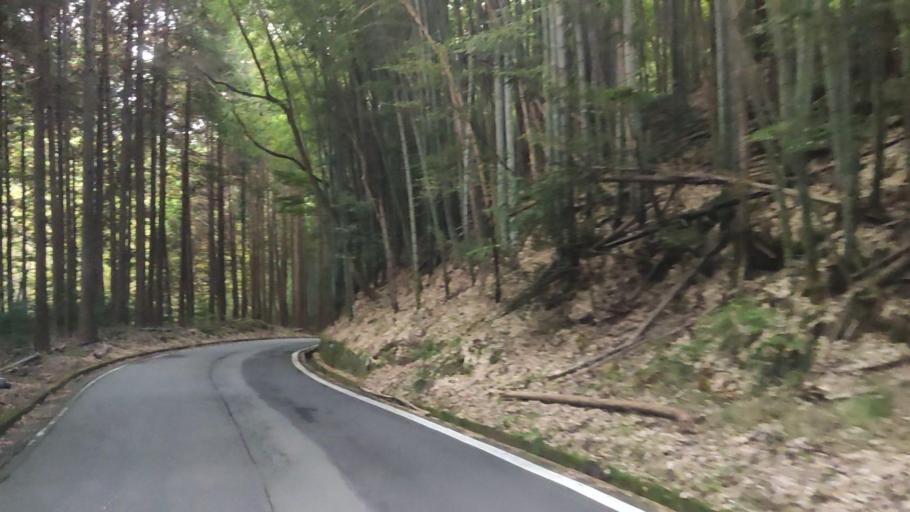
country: JP
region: Shizuoka
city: Ito
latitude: 34.9561
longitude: 139.0510
